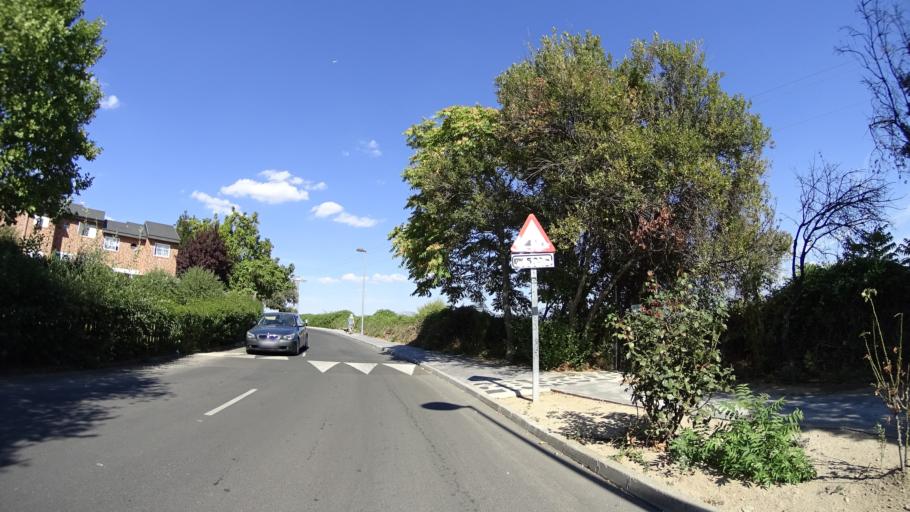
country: ES
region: Madrid
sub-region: Provincia de Madrid
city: Navalquejigo
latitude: 40.6078
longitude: -4.0251
